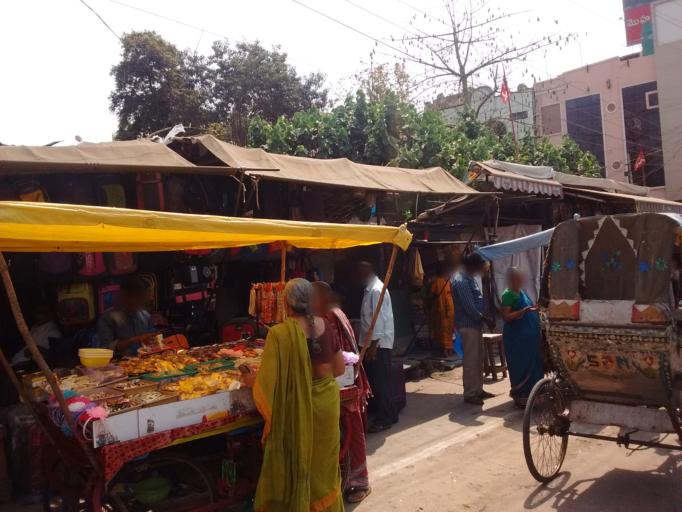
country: IN
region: Andhra Pradesh
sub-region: Krishna
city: Vijayawada
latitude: 16.5105
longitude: 80.6265
